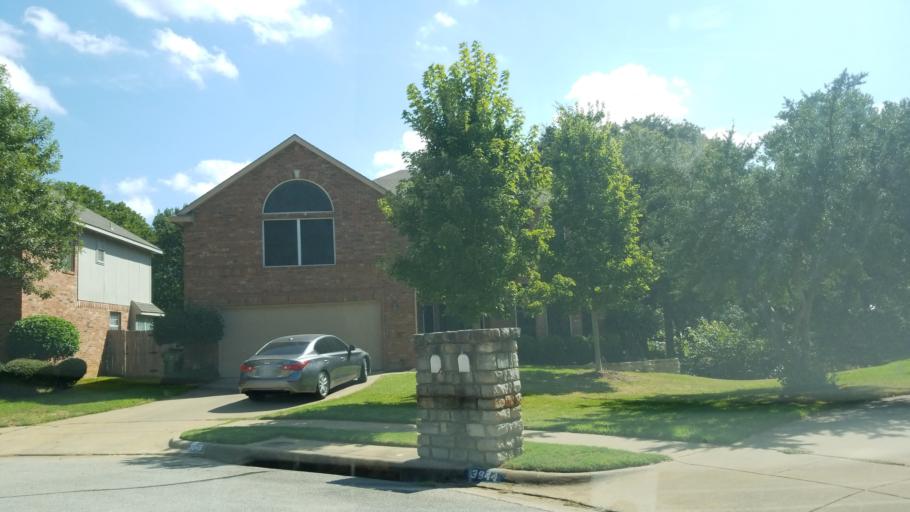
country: US
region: Texas
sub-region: Tarrant County
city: Euless
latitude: 32.8586
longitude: -97.1021
